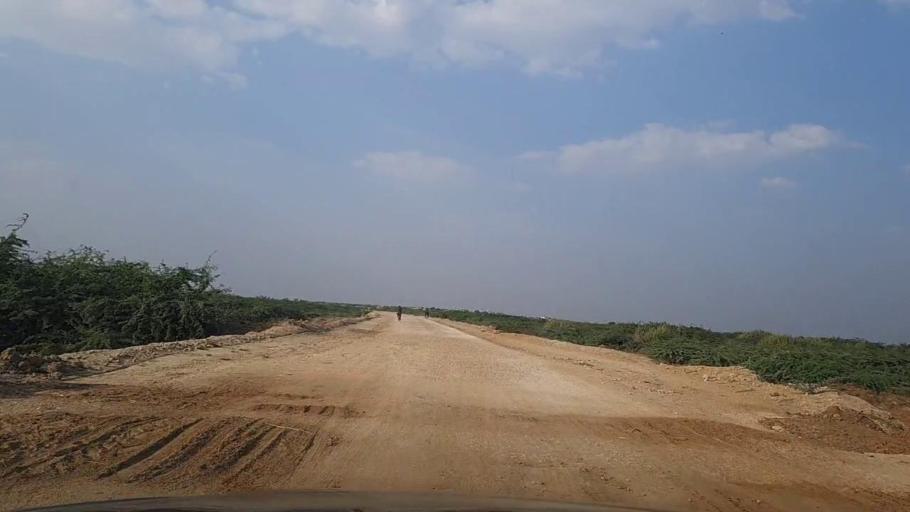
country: PK
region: Sindh
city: Gharo
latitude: 24.7942
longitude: 67.7448
